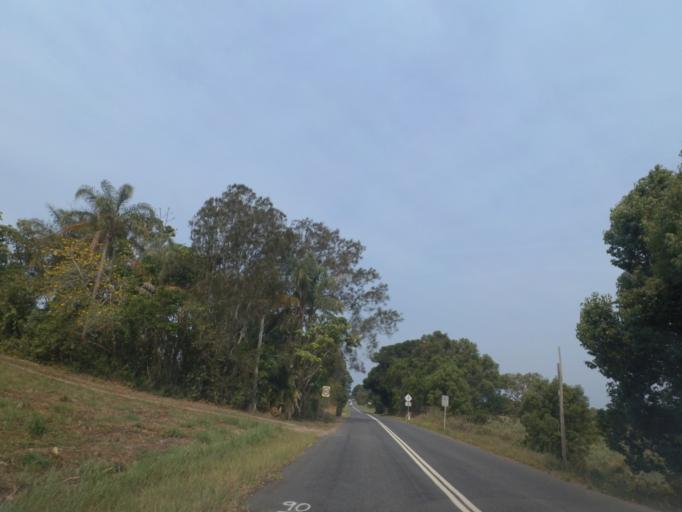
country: AU
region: New South Wales
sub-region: Tweed
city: Burringbar
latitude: -28.4548
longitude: 153.5361
